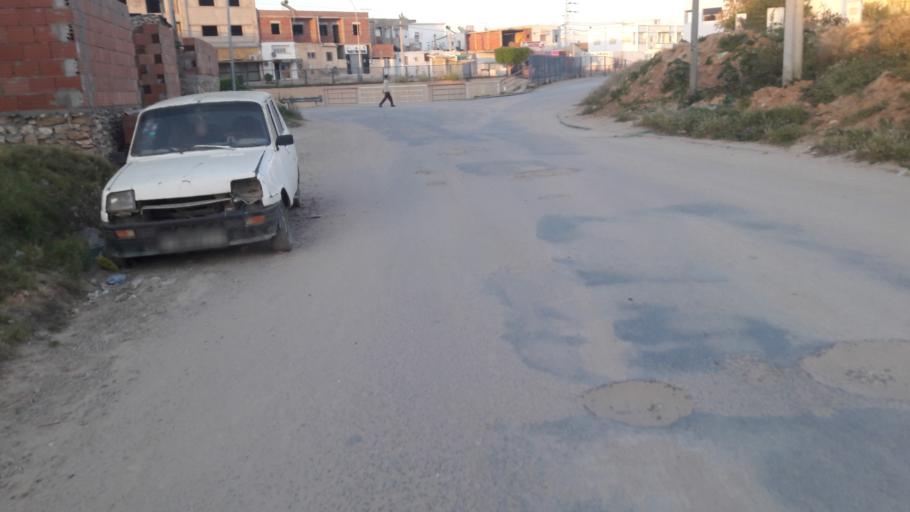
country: TN
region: Safaqis
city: Al Qarmadah
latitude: 34.8083
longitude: 10.7498
